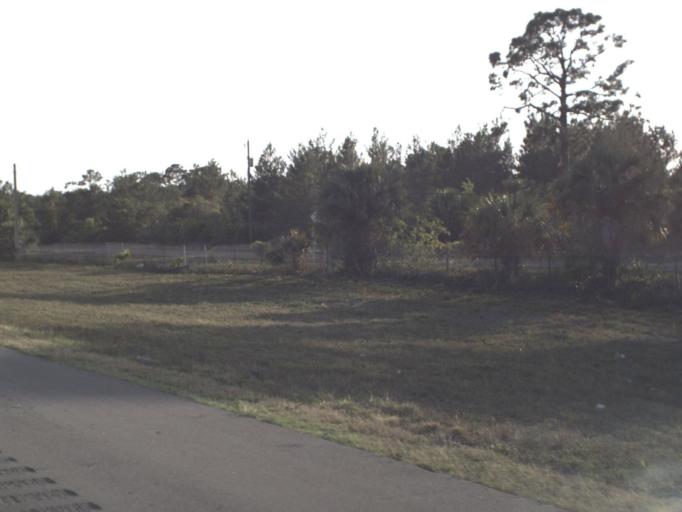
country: US
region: Florida
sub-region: Brevard County
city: Mims
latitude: 28.7324
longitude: -80.8865
